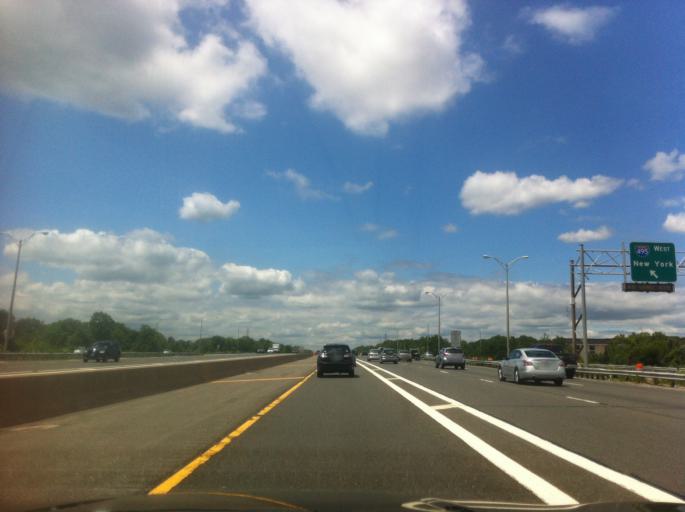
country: US
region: New York
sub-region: Suffolk County
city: Commack
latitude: 40.8050
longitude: -73.2889
